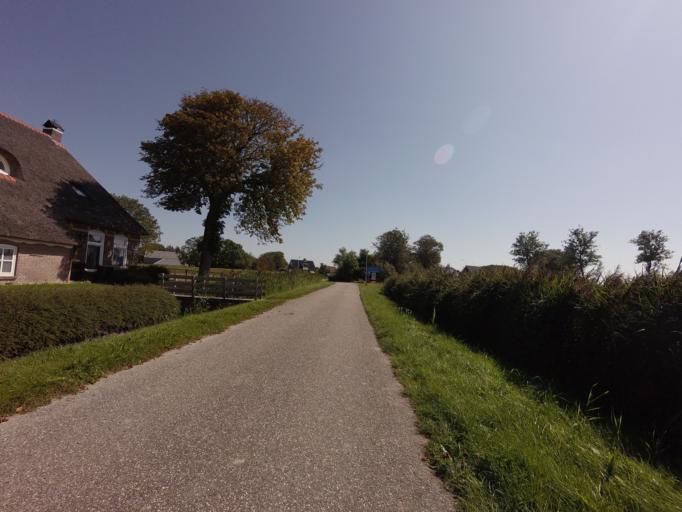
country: NL
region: Friesland
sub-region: Gemeente Dongeradeel
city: Dokkum
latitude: 53.3802
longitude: 6.0442
